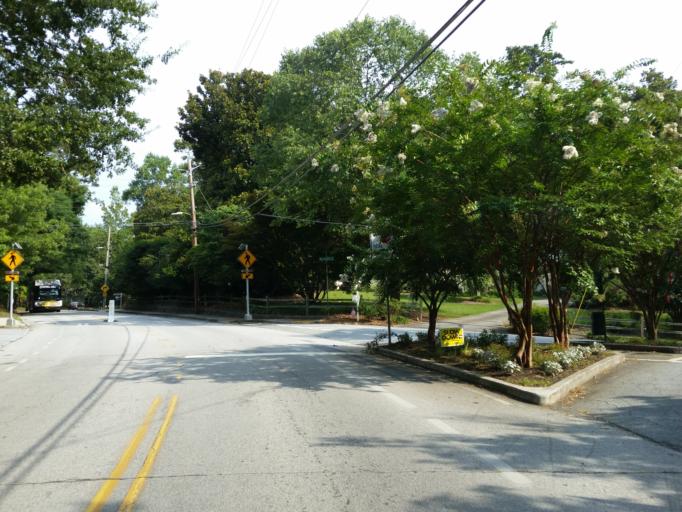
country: US
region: Georgia
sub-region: Cobb County
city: Vinings
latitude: 33.8187
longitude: -84.4169
